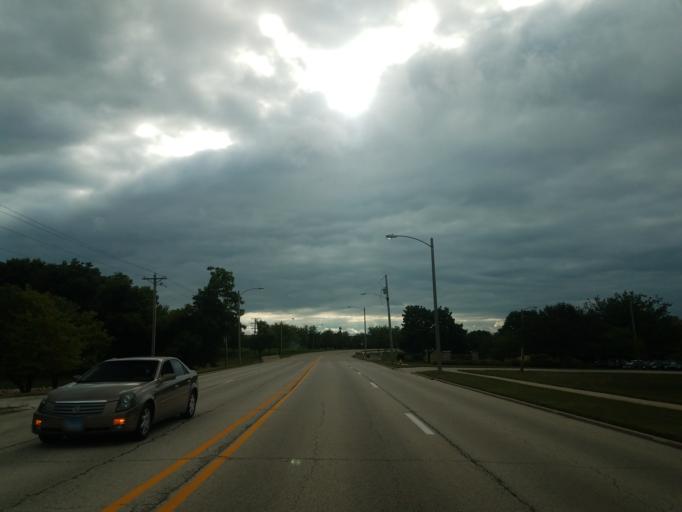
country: US
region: Illinois
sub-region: McLean County
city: Bloomington
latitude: 40.4589
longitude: -88.9468
